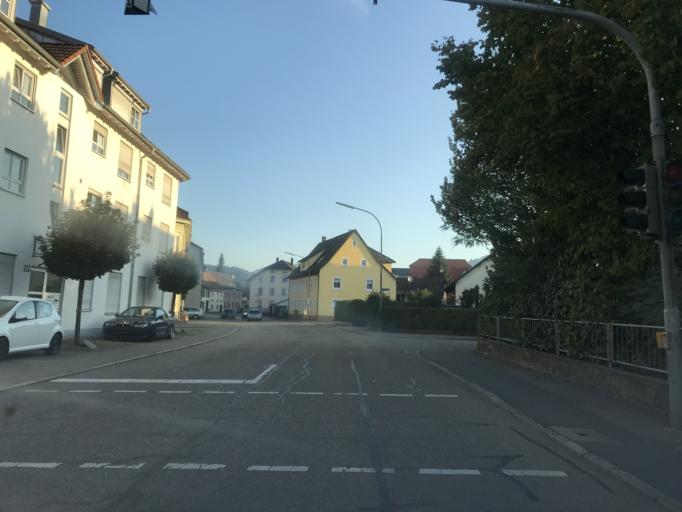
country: DE
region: Baden-Wuerttemberg
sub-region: Freiburg Region
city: Schopfheim
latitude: 47.6586
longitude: 7.8340
